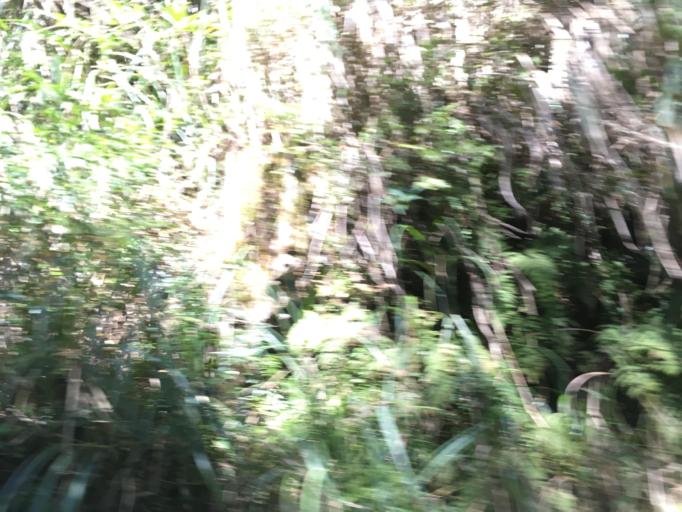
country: TW
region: Taiwan
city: Daxi
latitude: 24.5756
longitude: 121.4139
